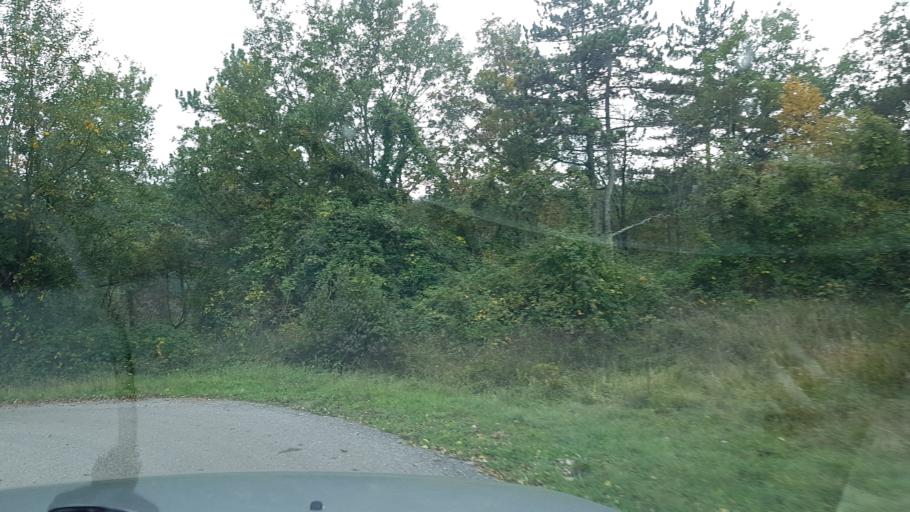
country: HR
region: Istarska
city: Buzet
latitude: 45.4422
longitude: 14.0477
